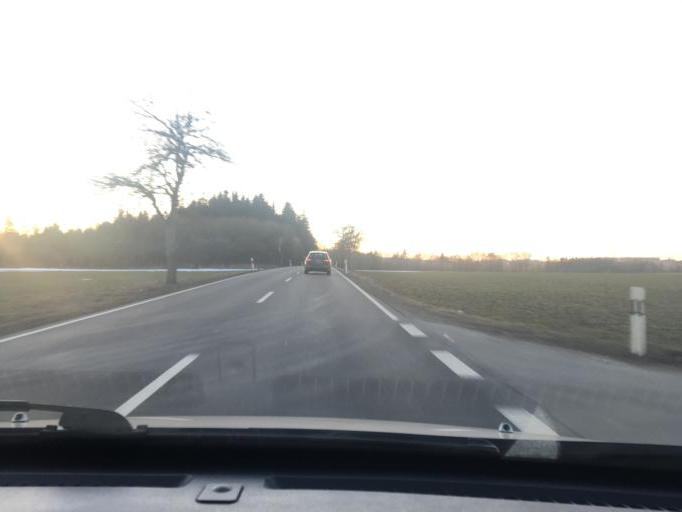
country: DE
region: Baden-Wuerttemberg
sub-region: Tuebingen Region
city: Erlenmoos
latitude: 48.0647
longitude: 10.0094
